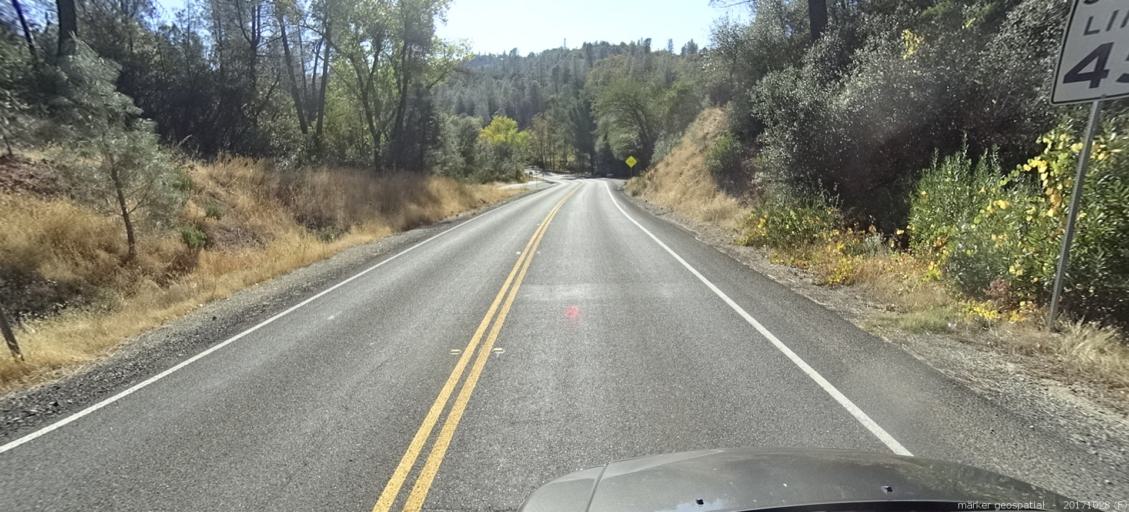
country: US
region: California
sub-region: Shasta County
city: Shasta
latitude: 40.5977
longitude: -122.4652
